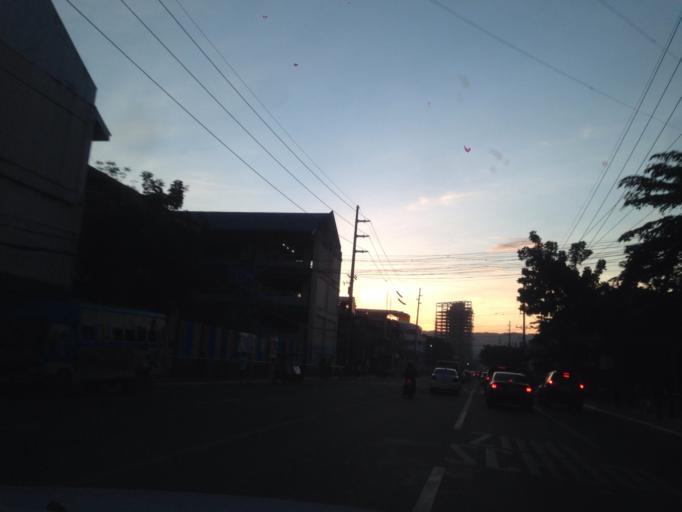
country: PH
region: Central Visayas
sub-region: Cebu City
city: Baugo
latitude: 10.3076
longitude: 123.9092
